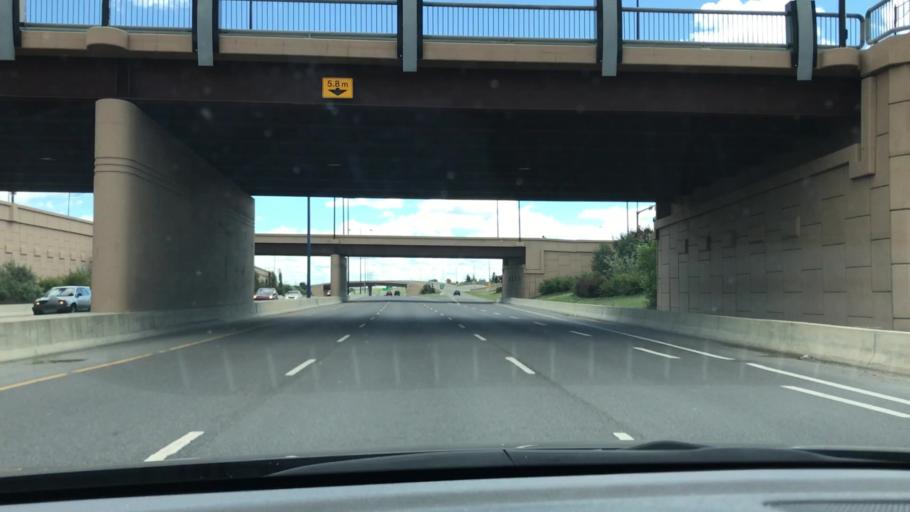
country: CA
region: Alberta
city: Edmonton
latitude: 53.4546
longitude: -113.4926
